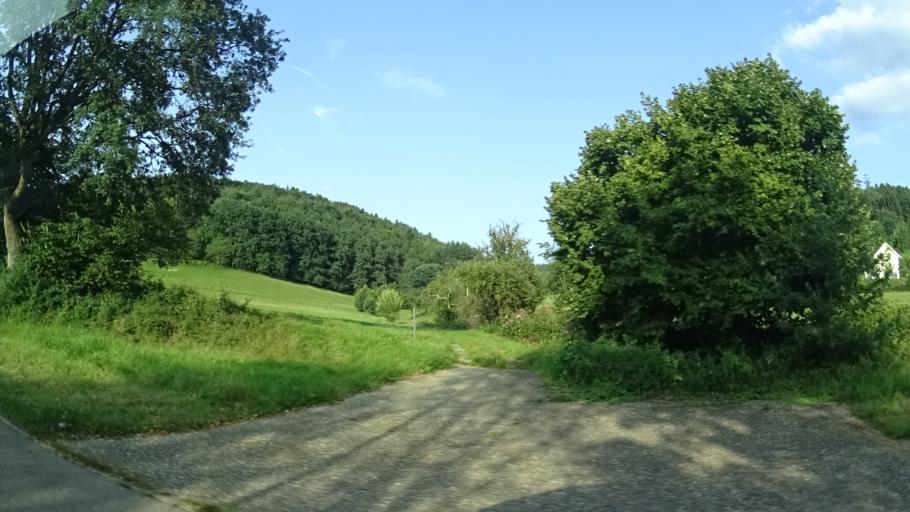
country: DE
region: Hesse
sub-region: Regierungsbezirk Darmstadt
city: Wald-Michelbach
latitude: 49.5323
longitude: 8.8647
